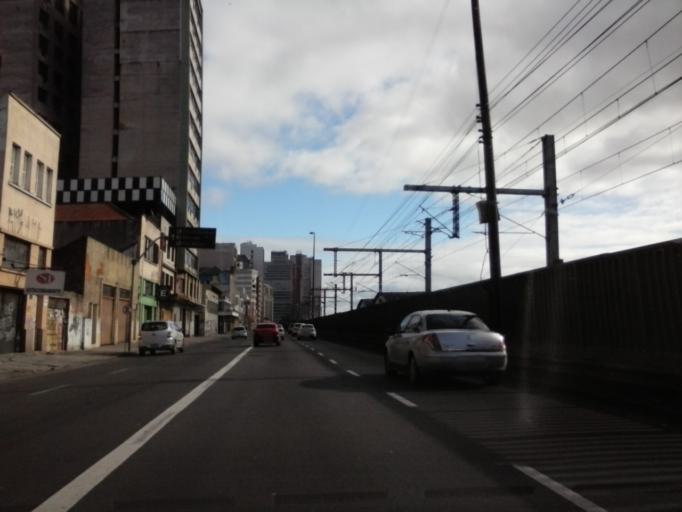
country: BR
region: Rio Grande do Sul
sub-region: Porto Alegre
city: Porto Alegre
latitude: -30.0239
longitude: -51.2224
